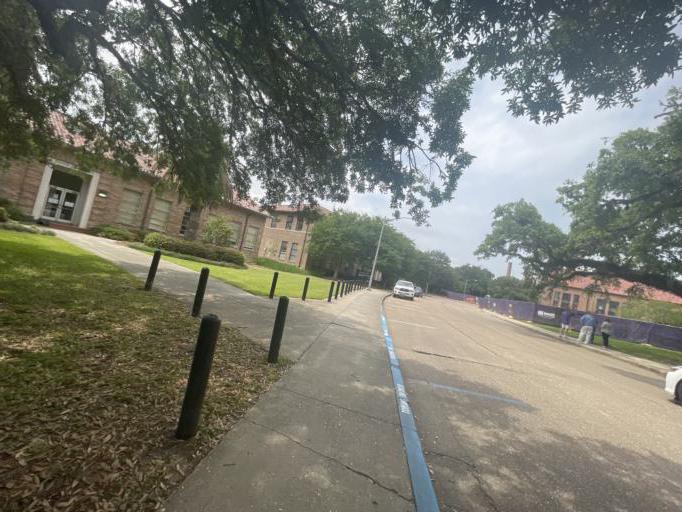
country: US
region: Louisiana
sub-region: East Baton Rouge Parish
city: Baton Rouge
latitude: 30.4111
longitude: -91.1788
